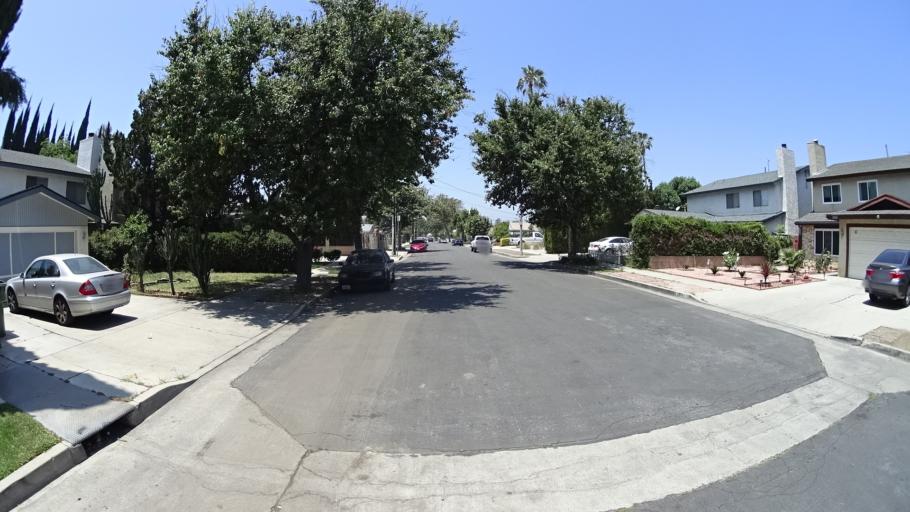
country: US
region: California
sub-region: Los Angeles County
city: Van Nuys
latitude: 34.2022
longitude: -118.4332
